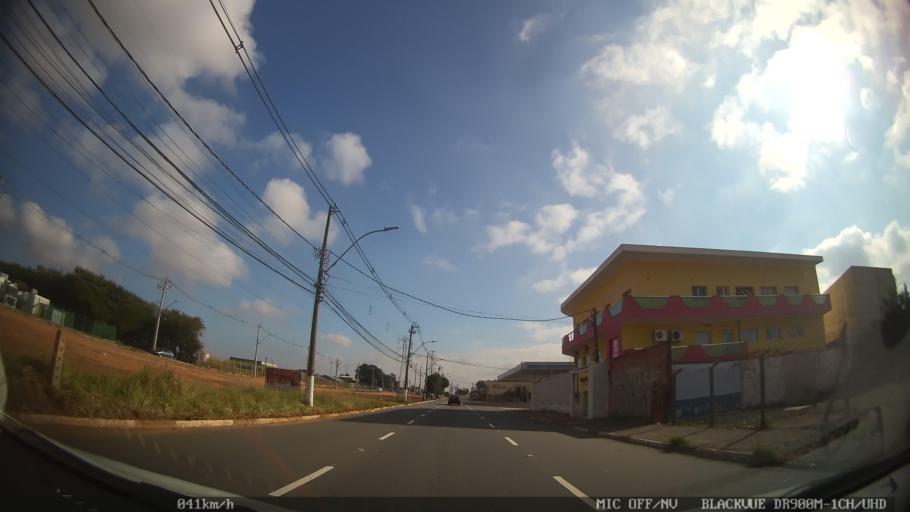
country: BR
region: Sao Paulo
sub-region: Hortolandia
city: Hortolandia
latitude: -22.8997
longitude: -47.1866
